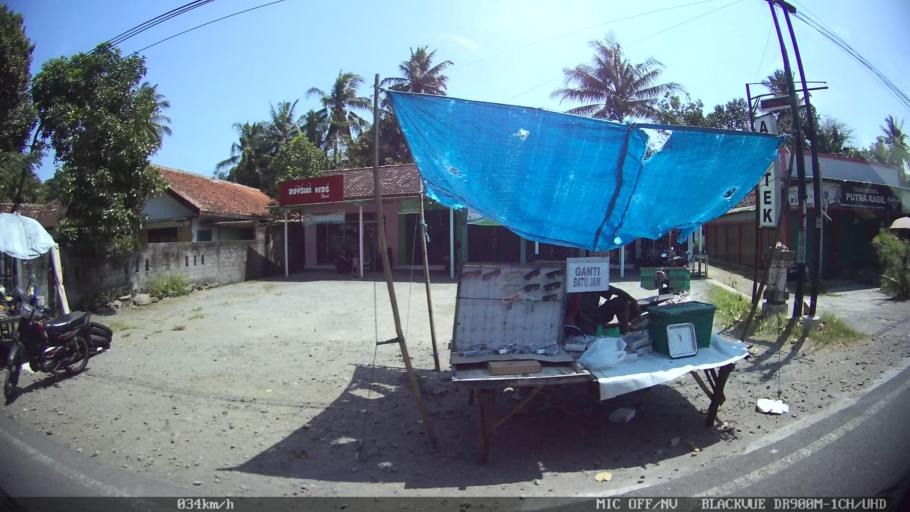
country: ID
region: Daerah Istimewa Yogyakarta
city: Srandakan
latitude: -7.9489
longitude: 110.2215
